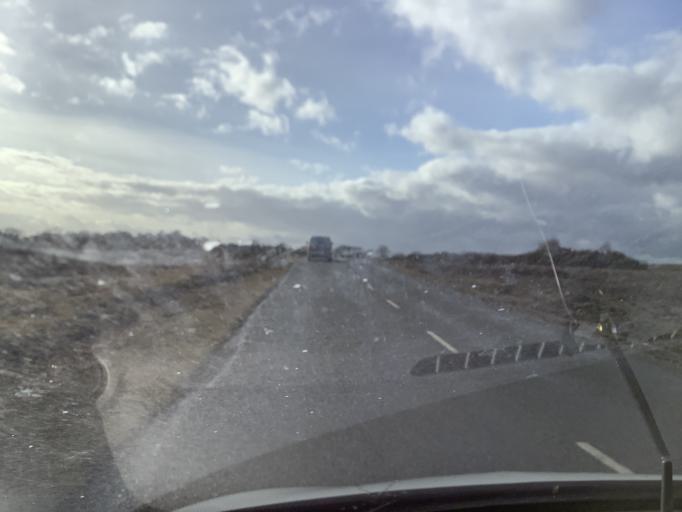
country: GB
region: England
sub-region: Hampshire
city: Hythe
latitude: 50.8274
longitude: -1.4221
